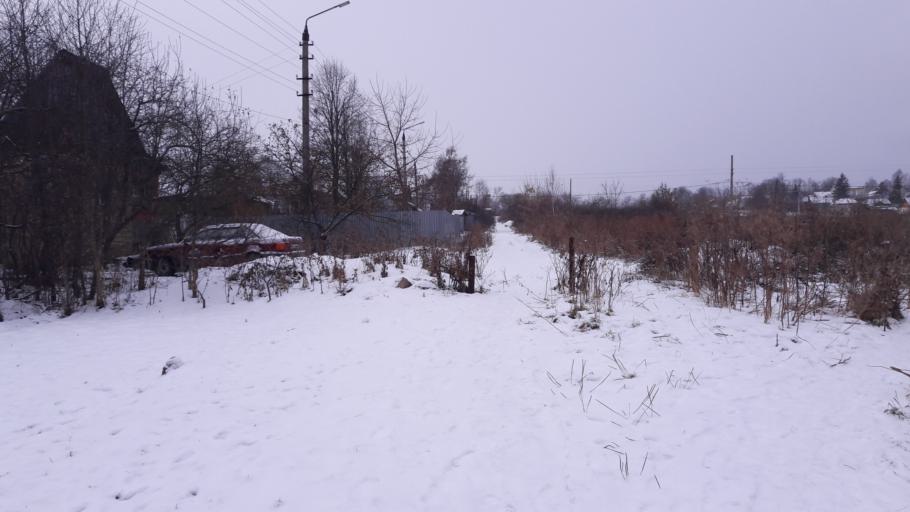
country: RU
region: Tula
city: Gorelki
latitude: 54.2362
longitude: 37.6361
